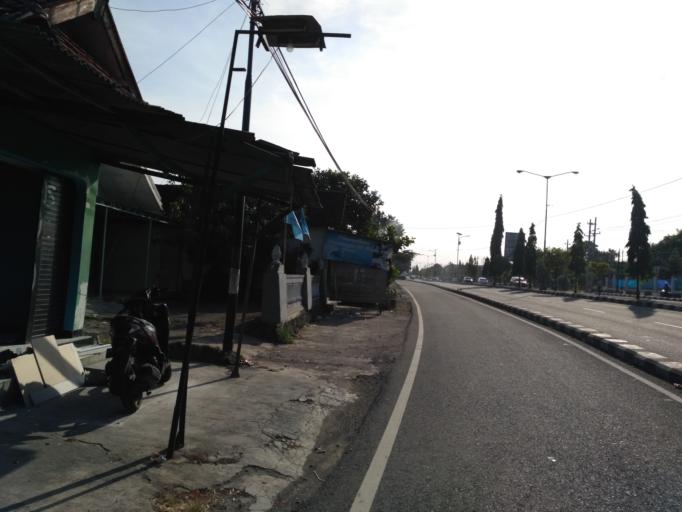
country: ID
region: Daerah Istimewa Yogyakarta
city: Depok
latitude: -7.7659
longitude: 110.4300
